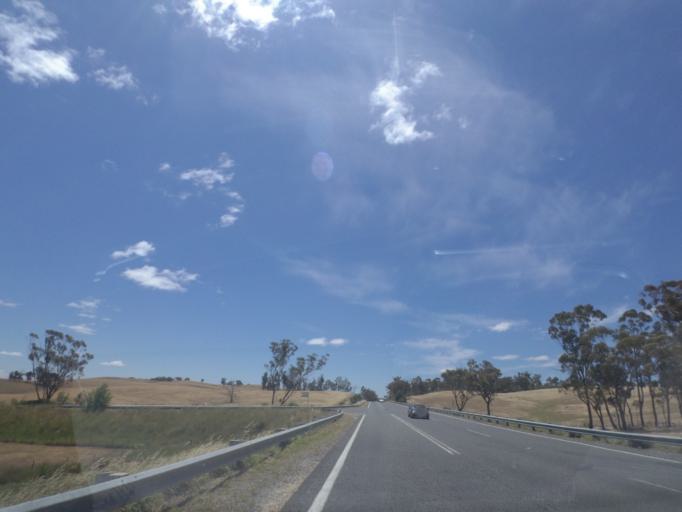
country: AU
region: Victoria
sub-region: Mount Alexander
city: Castlemaine
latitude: -37.2100
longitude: 144.1404
